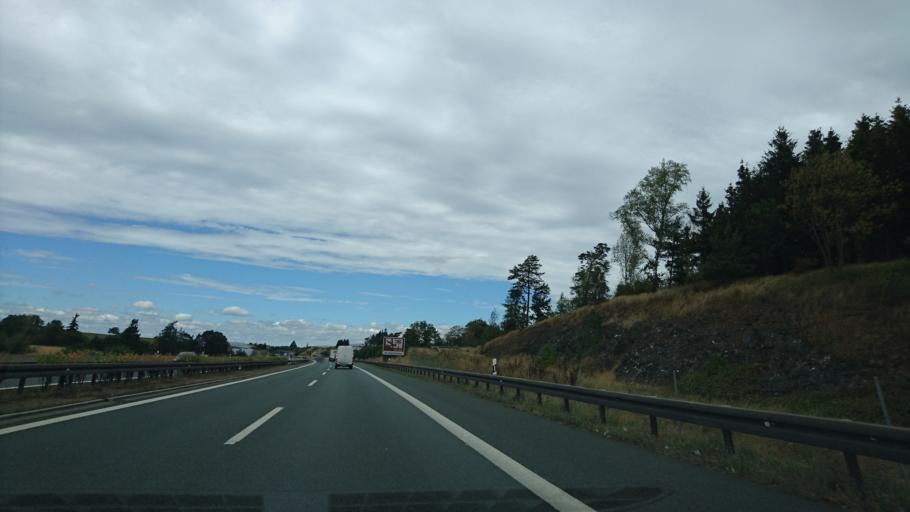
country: DE
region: Bavaria
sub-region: Upper Franconia
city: Gattendorf
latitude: 50.3415
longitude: 12.0056
